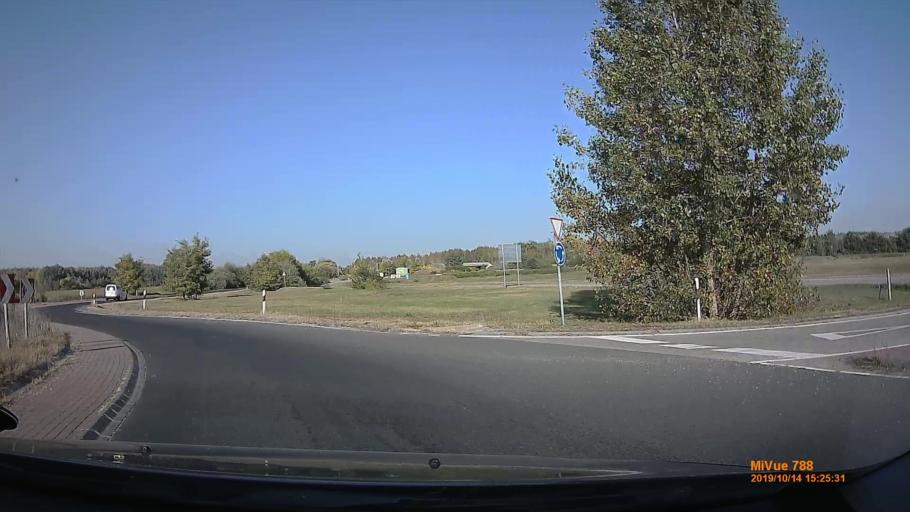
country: HU
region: Pest
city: Vecses
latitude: 47.4104
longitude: 19.3112
